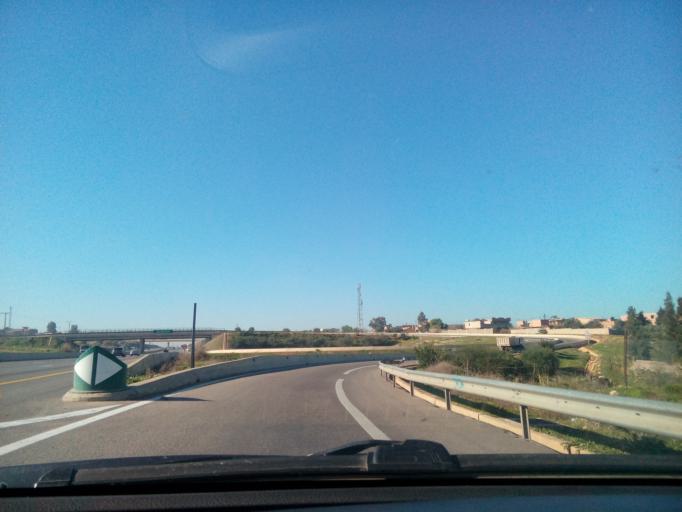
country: DZ
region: Chlef
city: Boukadir
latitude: 36.0554
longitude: 1.1390
